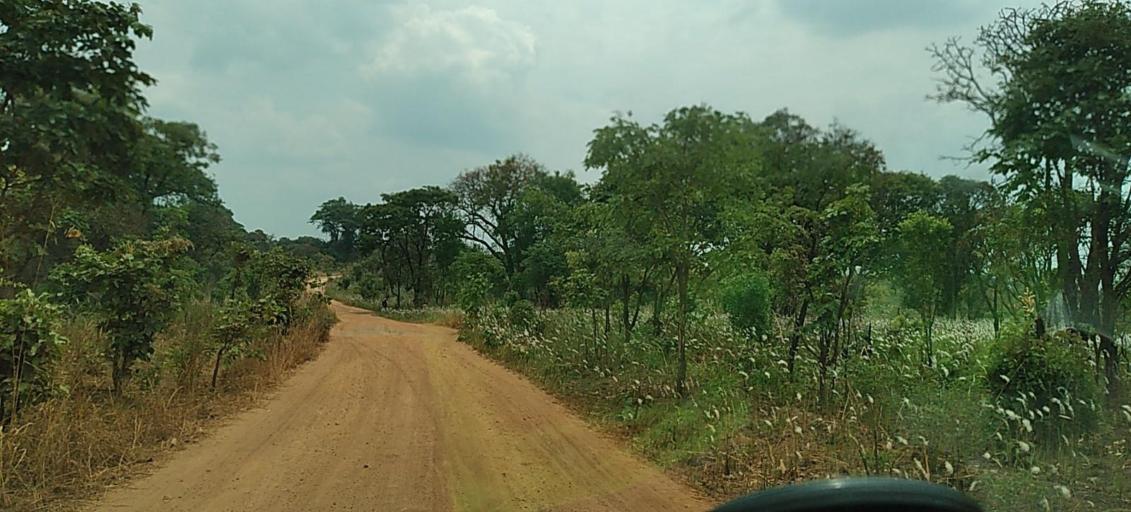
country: ZM
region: North-Western
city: Kansanshi
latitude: -12.0600
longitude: 26.3498
